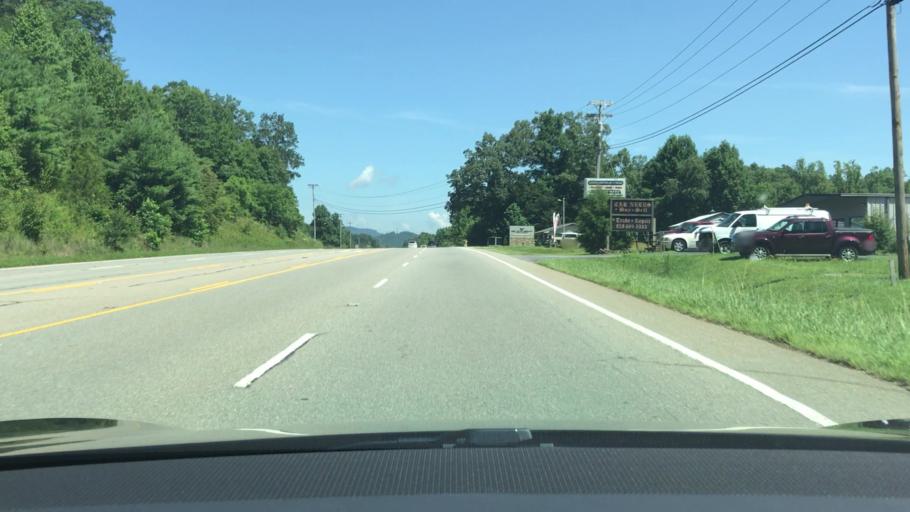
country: US
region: North Carolina
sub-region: Macon County
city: Franklin
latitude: 35.1040
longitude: -83.3861
